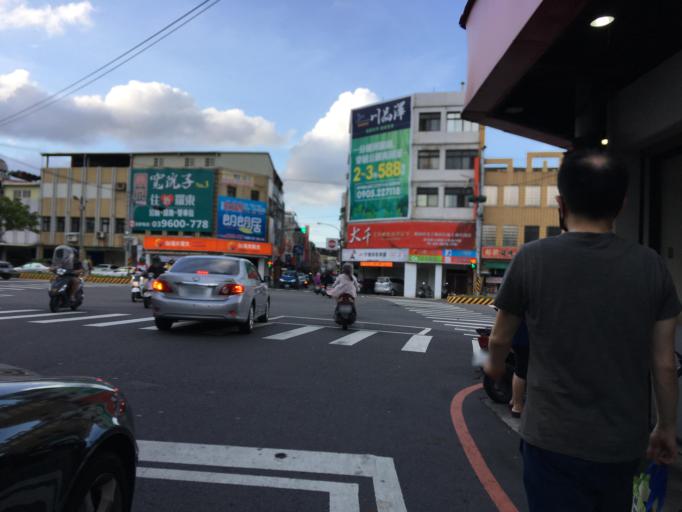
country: TW
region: Taiwan
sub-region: Yilan
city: Yilan
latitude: 24.6676
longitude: 121.7681
